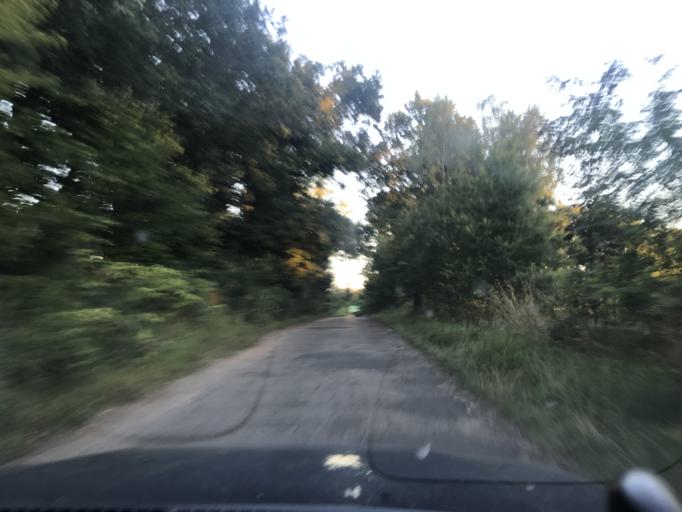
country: PL
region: West Pomeranian Voivodeship
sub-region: Powiat stargardzki
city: Chociwel
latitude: 53.4680
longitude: 15.3717
